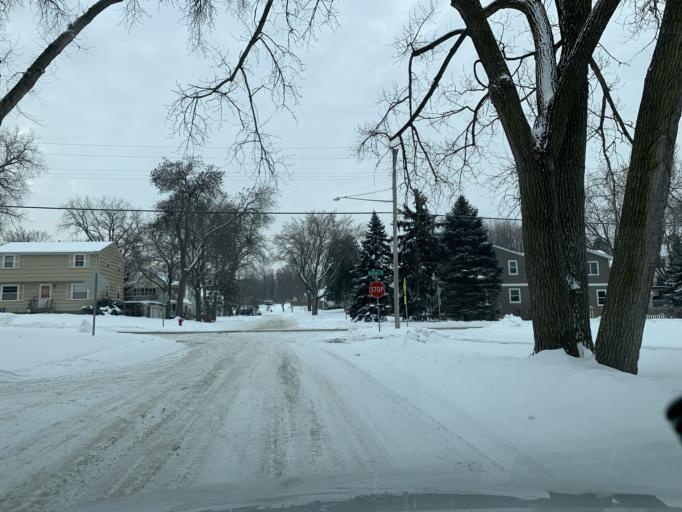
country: US
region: Minnesota
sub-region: Hennepin County
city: Edina
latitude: 44.9172
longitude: -93.3556
